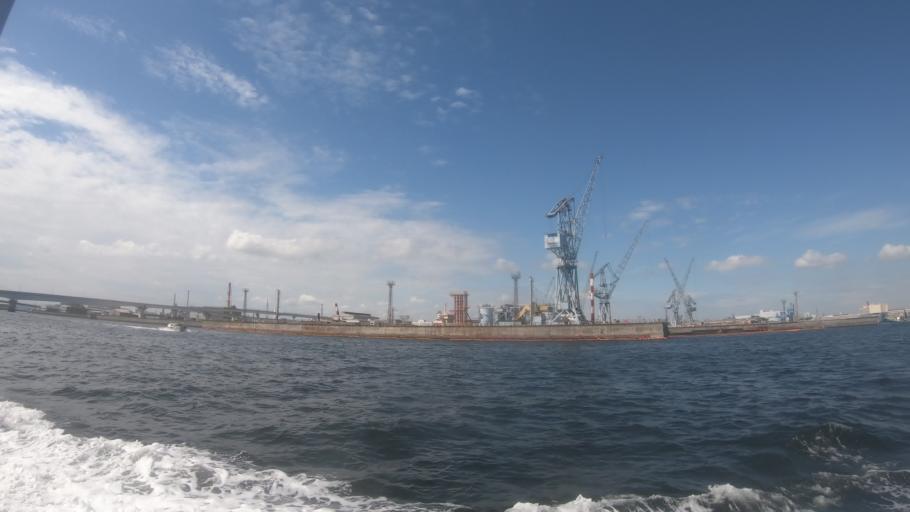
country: JP
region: Kanagawa
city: Yokohama
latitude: 35.4163
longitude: 139.6850
